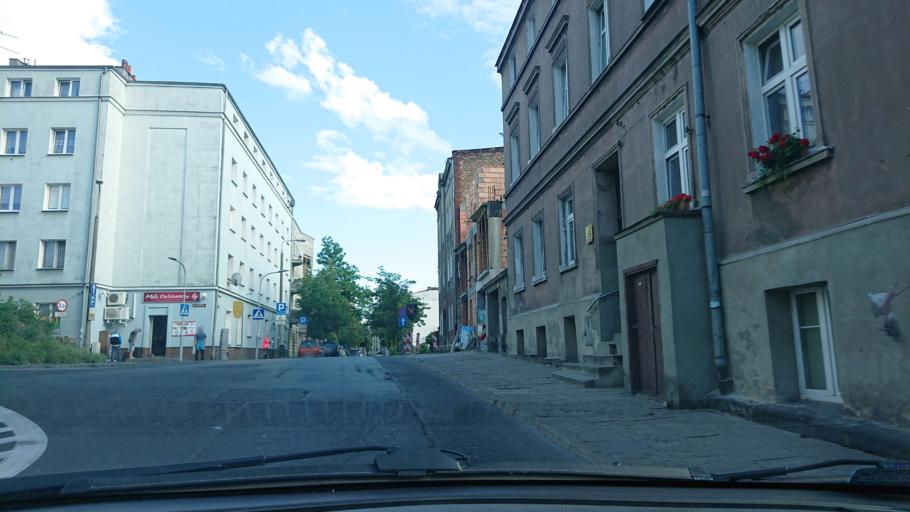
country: PL
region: Greater Poland Voivodeship
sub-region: Powiat gnieznienski
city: Gniezno
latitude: 52.5323
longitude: 17.5917
